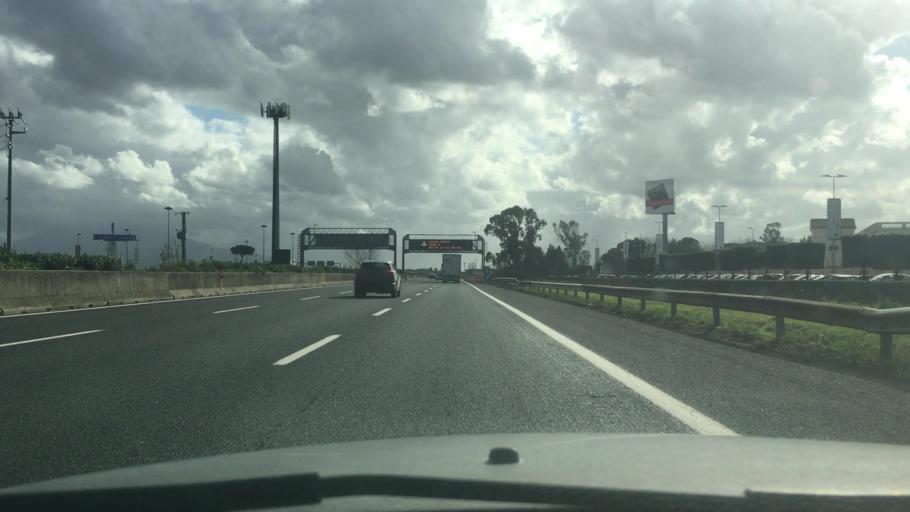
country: IT
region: Campania
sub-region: Provincia di Caserta
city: Marcianise
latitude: 41.0078
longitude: 14.3231
